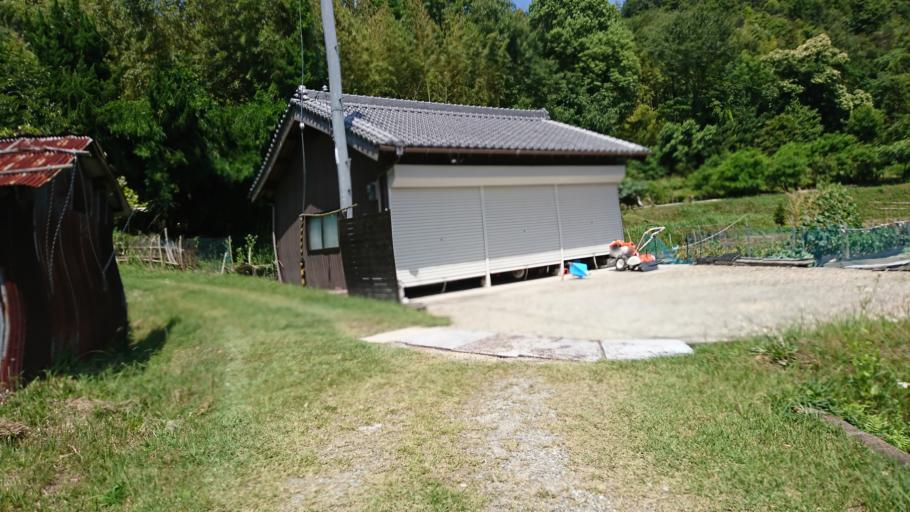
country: JP
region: Hyogo
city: Kakogawacho-honmachi
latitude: 34.8095
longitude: 134.7853
